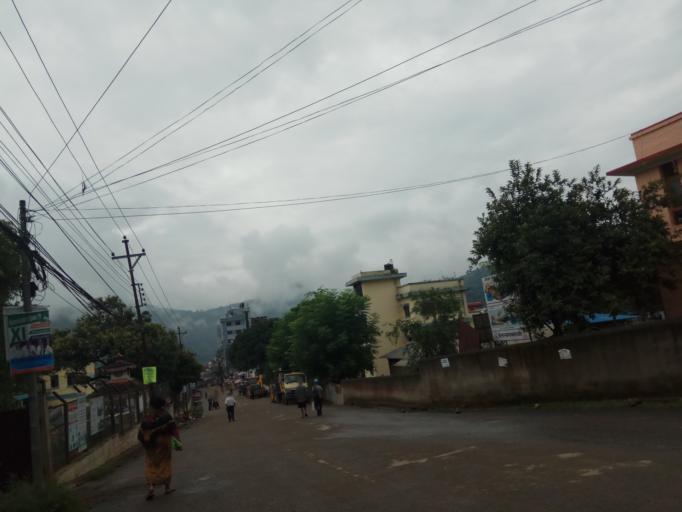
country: NP
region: Central Region
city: Kirtipur
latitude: 27.9108
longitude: 84.8953
